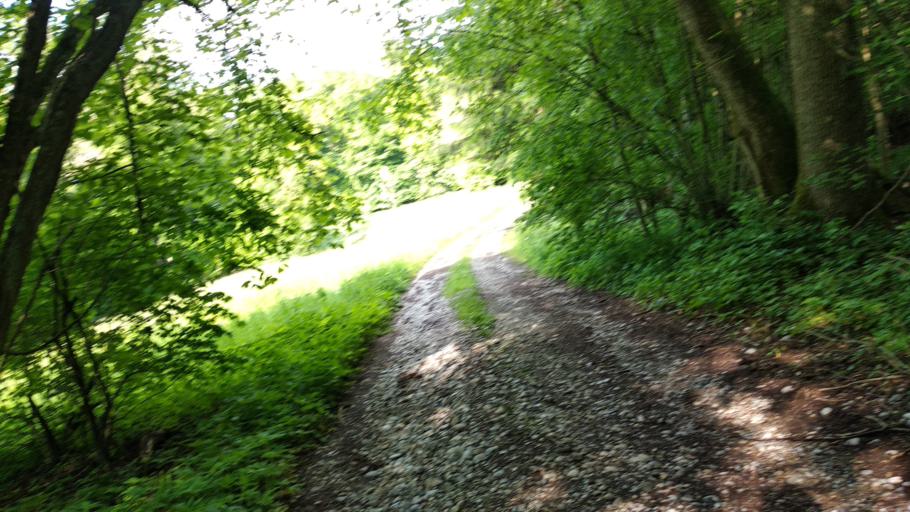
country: DE
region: Bavaria
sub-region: Swabia
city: Kronburg
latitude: 47.8836
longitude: 10.1503
